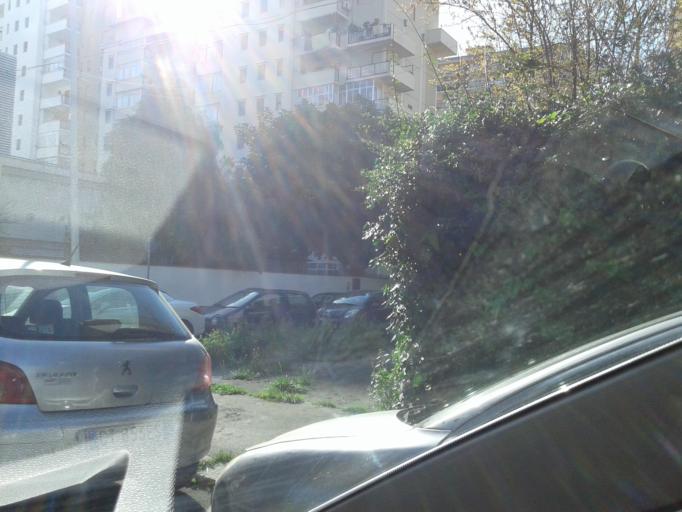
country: IT
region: Sicily
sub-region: Palermo
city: Palermo
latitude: 38.1280
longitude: 13.3319
